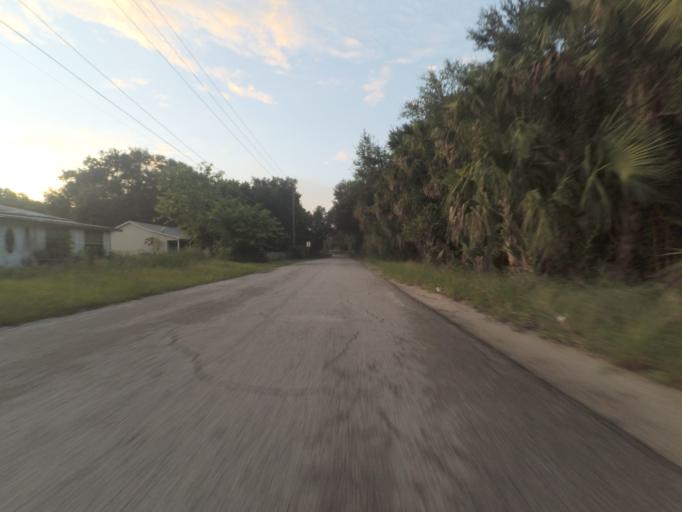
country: US
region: Florida
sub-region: Lake County
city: Umatilla
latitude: 28.9152
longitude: -81.6707
